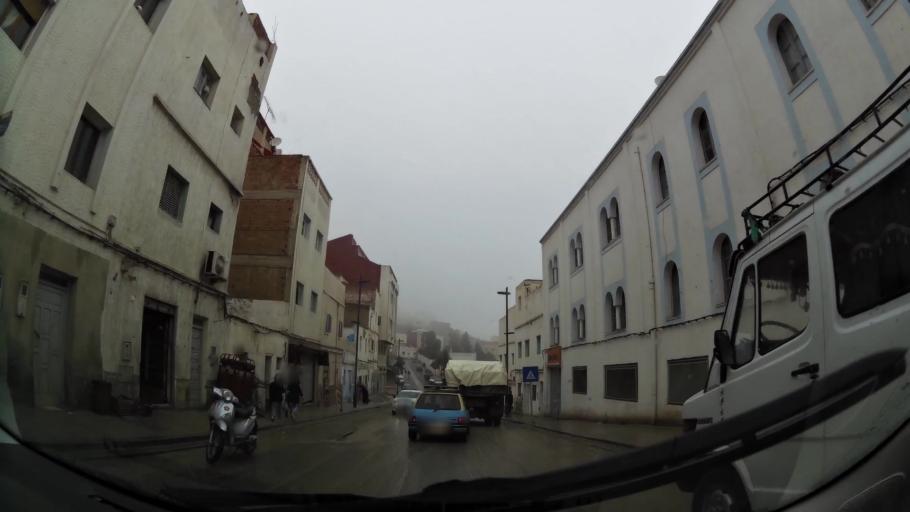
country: MA
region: Taza-Al Hoceima-Taounate
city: Al Hoceima
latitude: 35.2378
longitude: -3.9391
